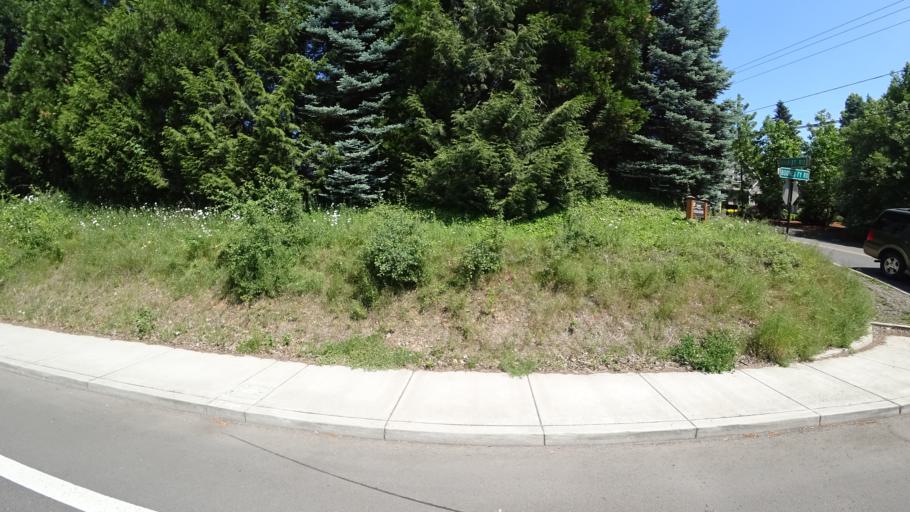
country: US
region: Oregon
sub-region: Clackamas County
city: Lake Oswego
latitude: 45.4316
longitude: -122.7026
